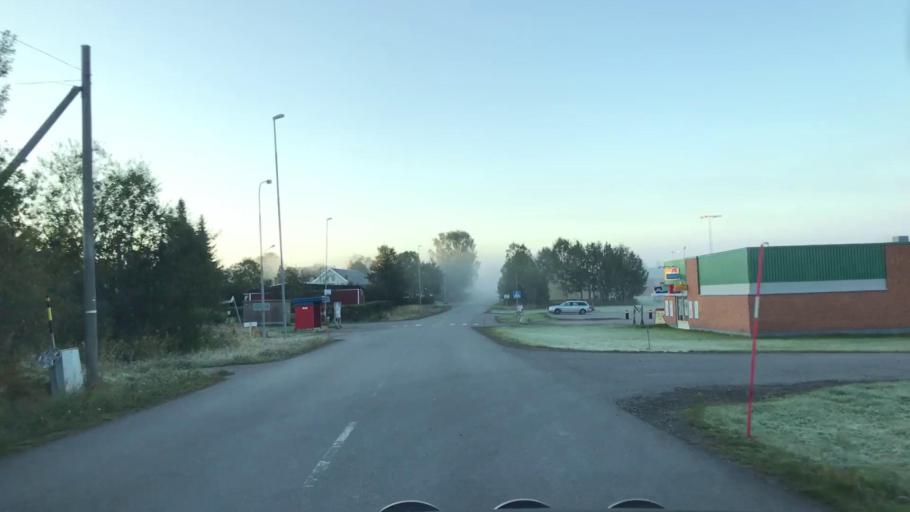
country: SE
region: Norrbotten
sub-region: Gallivare Kommun
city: Malmberget
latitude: 67.6489
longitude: 21.0460
